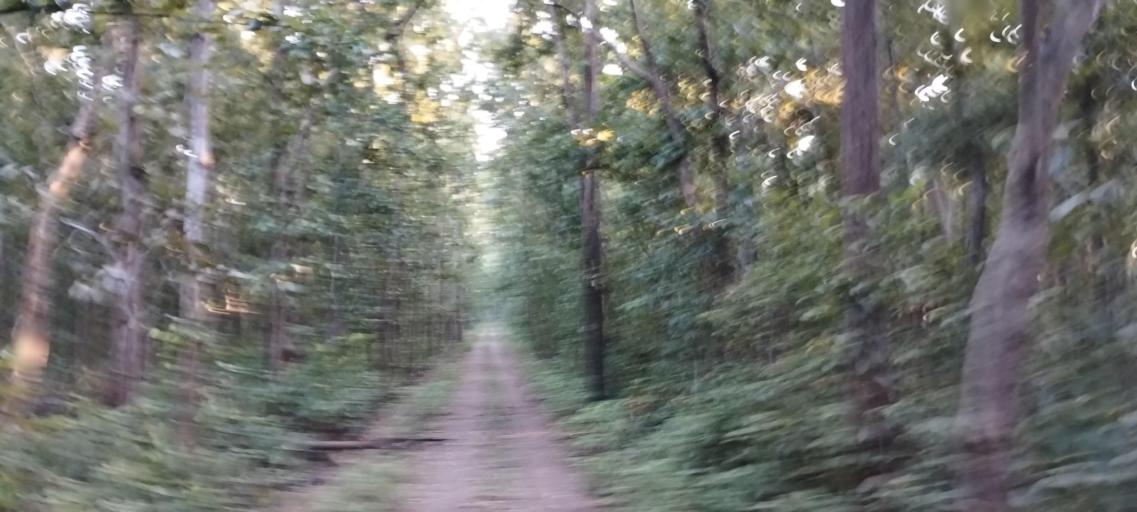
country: NP
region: Far Western
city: Tikapur
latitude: 28.4832
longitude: 81.2618
